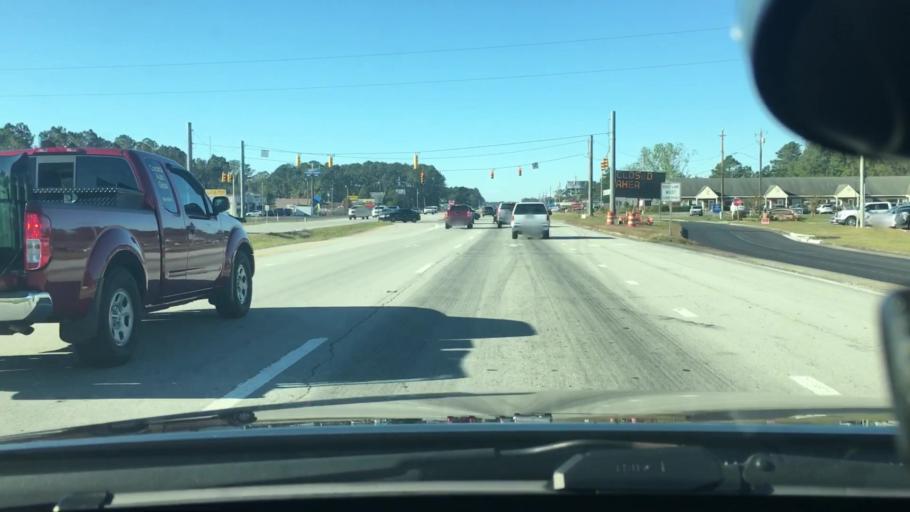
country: US
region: North Carolina
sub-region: Craven County
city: Havelock
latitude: 34.8958
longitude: -76.9269
